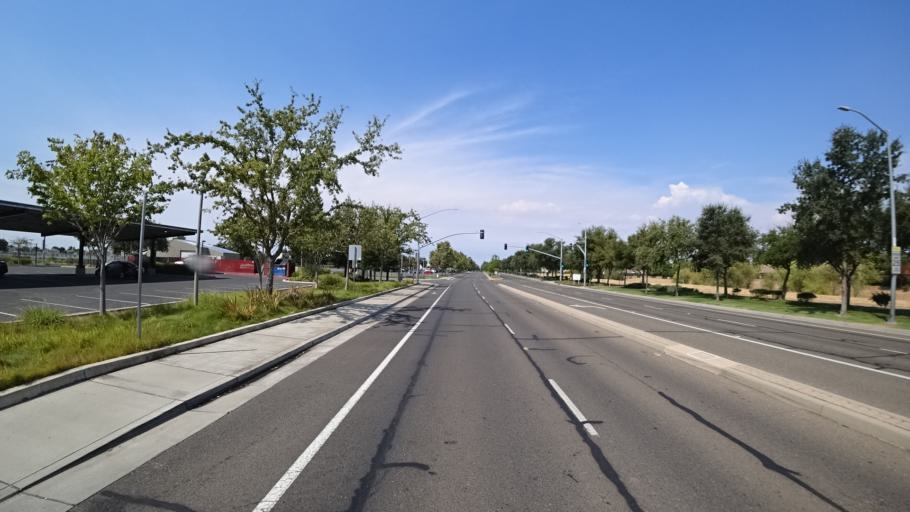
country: US
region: California
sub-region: Sacramento County
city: Laguna
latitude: 38.3939
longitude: -121.4263
